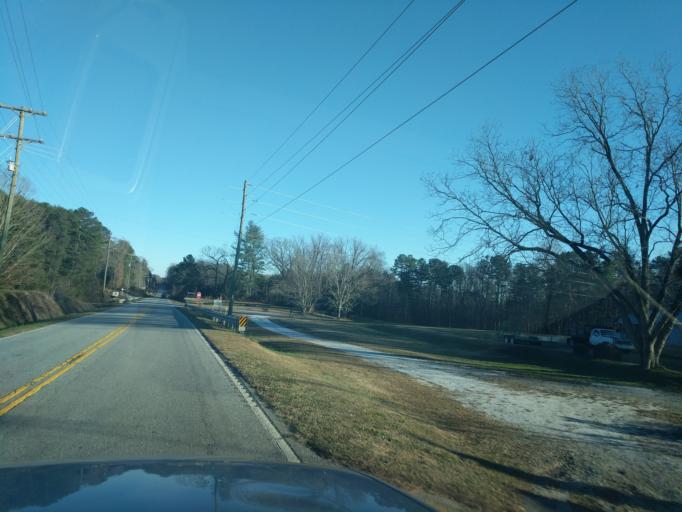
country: US
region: South Carolina
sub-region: Oconee County
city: Westminster
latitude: 34.6909
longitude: -83.1786
